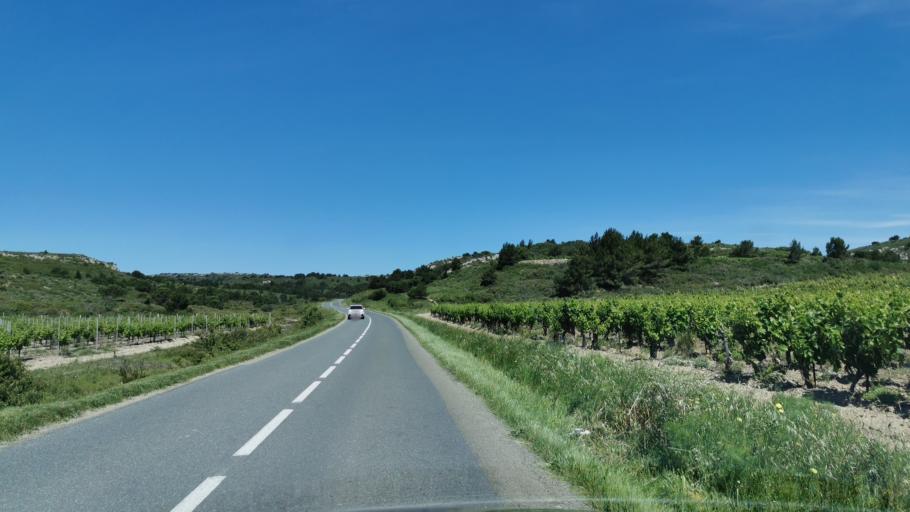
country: FR
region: Languedoc-Roussillon
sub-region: Departement de l'Aude
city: Armissan
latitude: 43.1592
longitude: 3.1499
